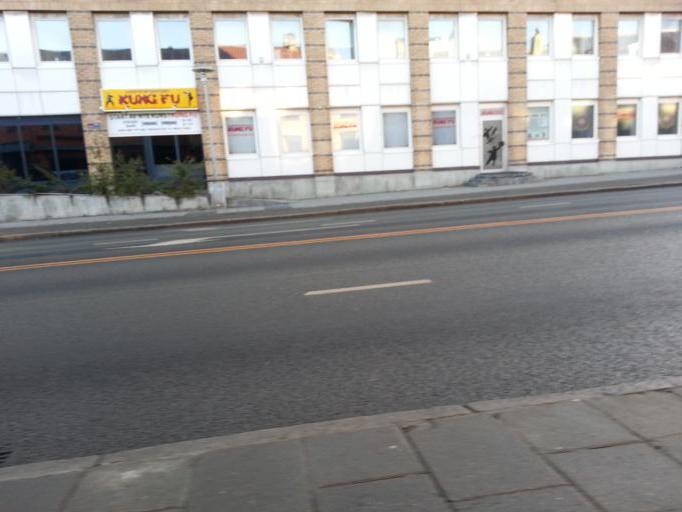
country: NO
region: Sor-Trondelag
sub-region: Trondheim
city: Trondheim
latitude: 63.4327
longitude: 10.3916
